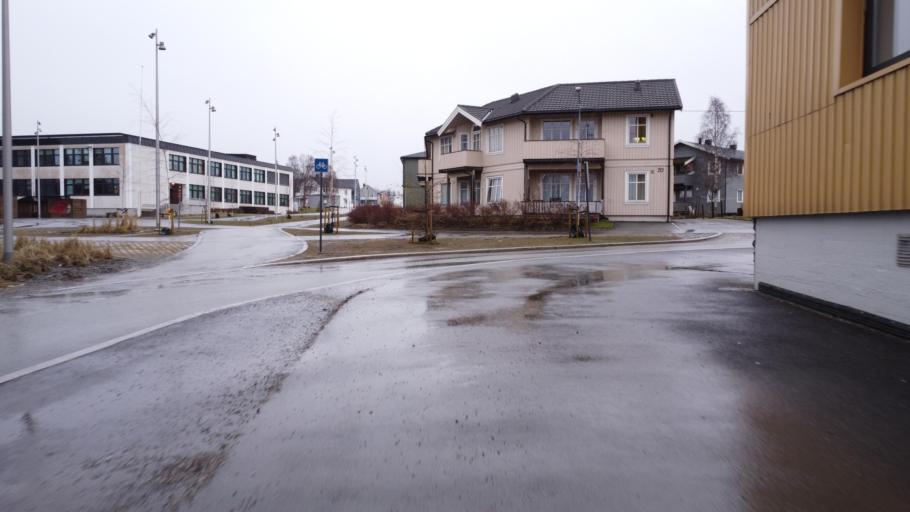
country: NO
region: Nordland
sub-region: Rana
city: Mo i Rana
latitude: 66.3113
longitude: 14.1452
